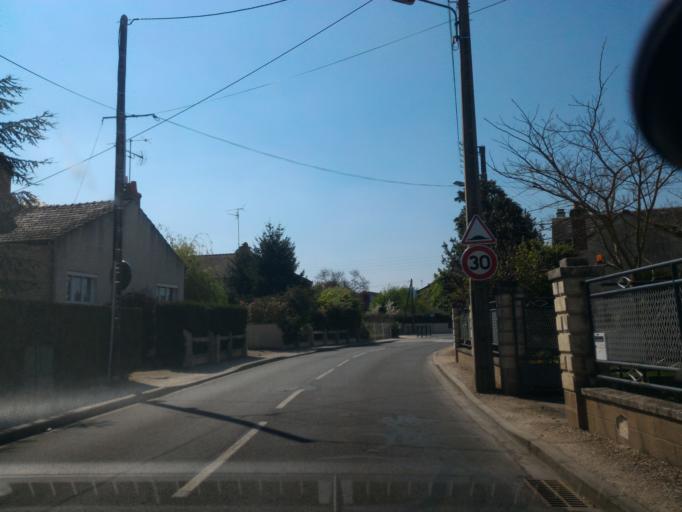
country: FR
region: Centre
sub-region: Departement du Loiret
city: Saint-Jean-le-Blanc
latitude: 47.8892
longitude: 1.9148
